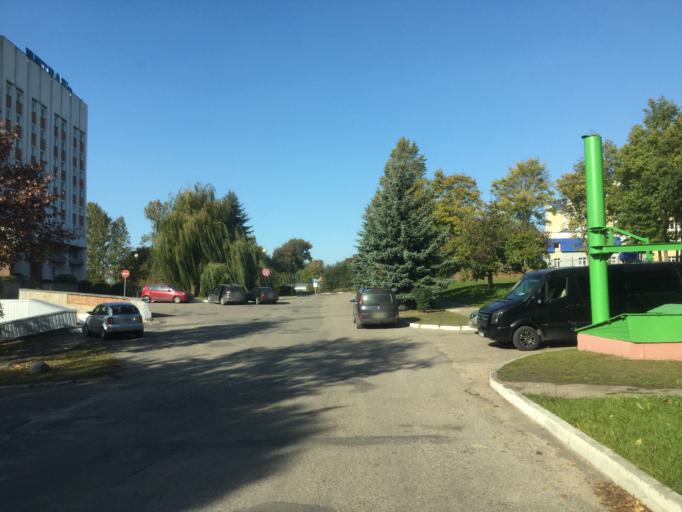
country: BY
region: Vitebsk
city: Vitebsk
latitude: 55.1739
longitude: 30.1955
